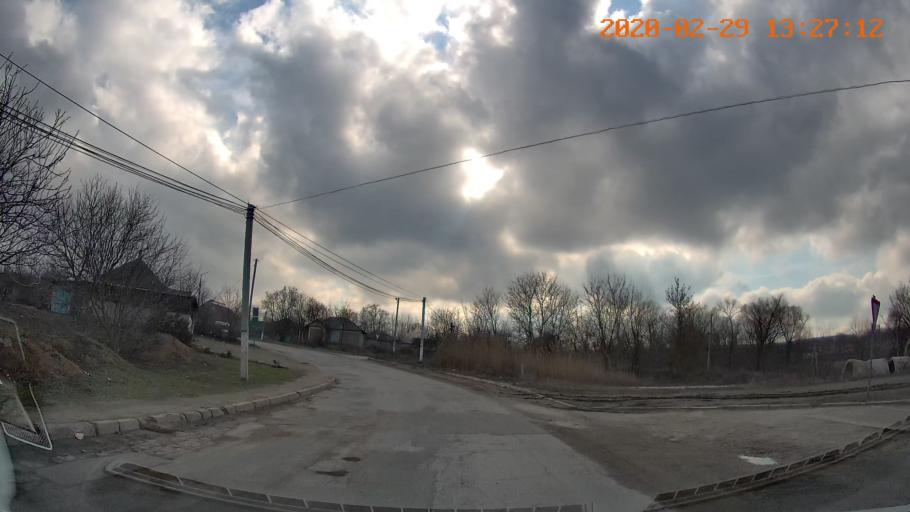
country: MD
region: Telenesti
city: Camenca
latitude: 47.9136
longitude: 28.6396
